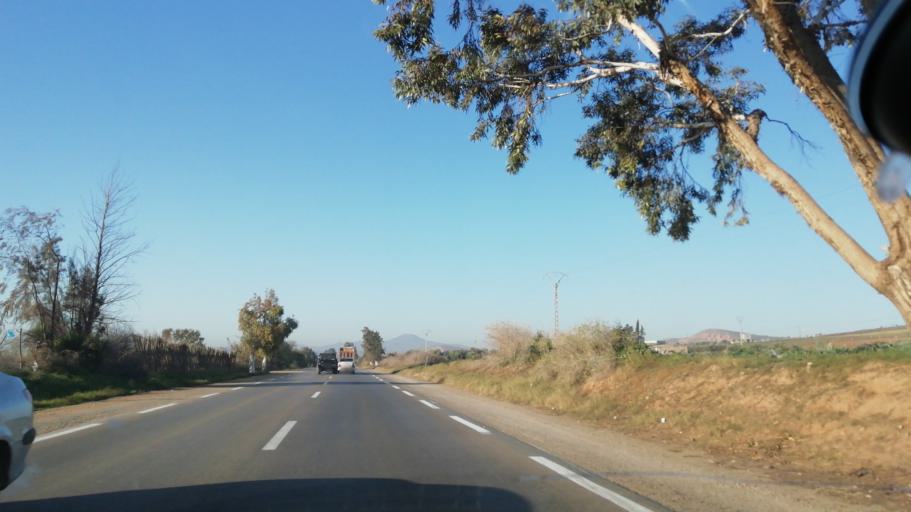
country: DZ
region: Tlemcen
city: Remchi
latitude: 35.0640
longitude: -1.4827
